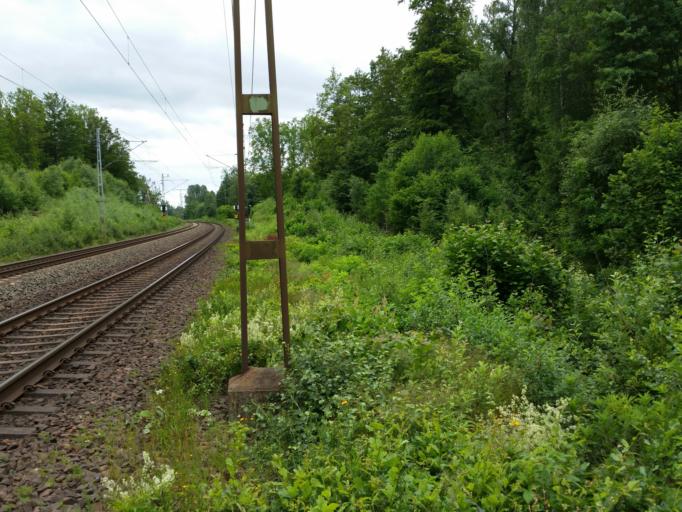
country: SE
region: Kronoberg
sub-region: Almhults Kommun
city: AElmhult
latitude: 56.5700
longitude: 14.1444
